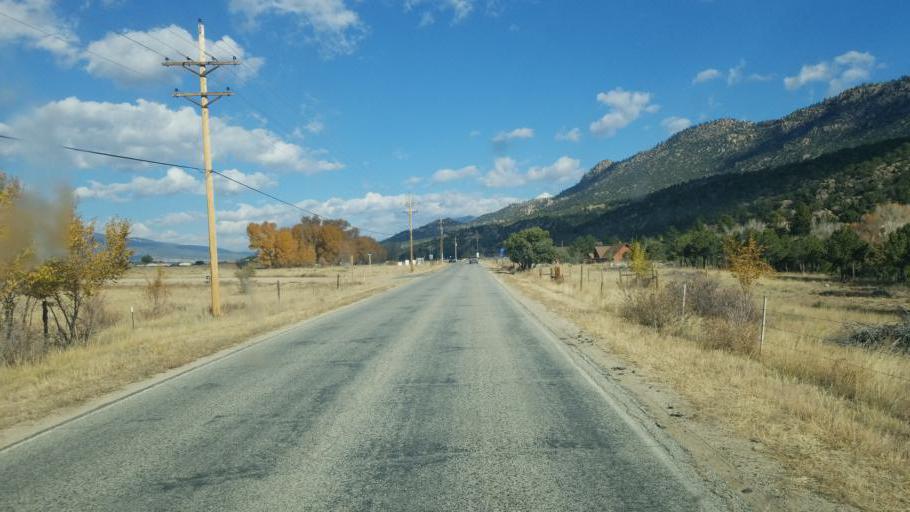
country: US
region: Colorado
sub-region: Chaffee County
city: Buena Vista
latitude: 38.8253
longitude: -106.1099
